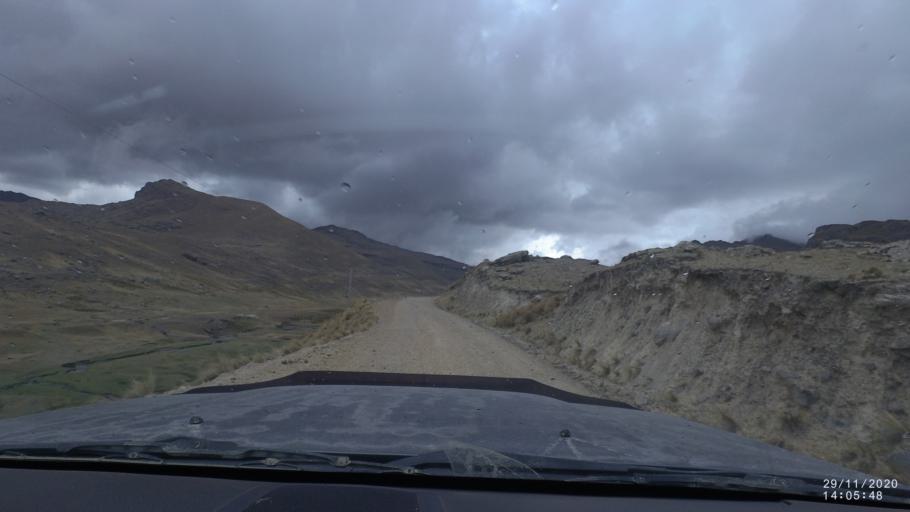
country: BO
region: Cochabamba
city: Sipe Sipe
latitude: -17.2089
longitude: -66.3766
